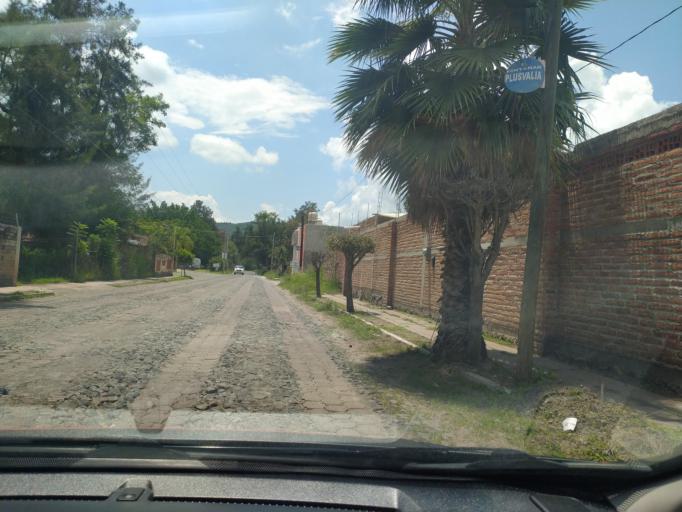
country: MX
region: Jalisco
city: Villa Corona
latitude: 20.4125
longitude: -103.6703
